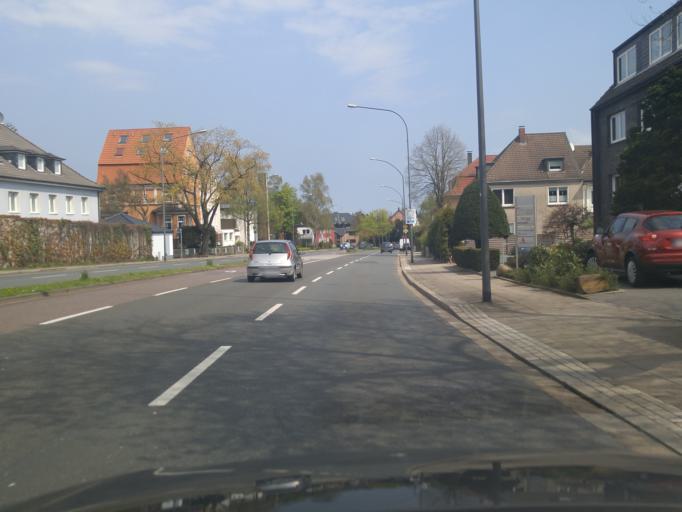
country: DE
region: North Rhine-Westphalia
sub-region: Regierungsbezirk Dusseldorf
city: Essen
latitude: 51.4170
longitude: 6.9953
